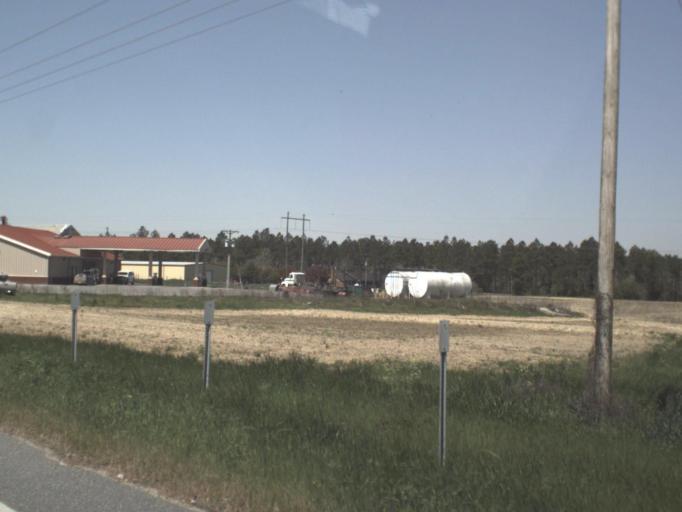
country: US
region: Florida
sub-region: Jackson County
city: Graceville
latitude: 30.9647
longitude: -85.5782
